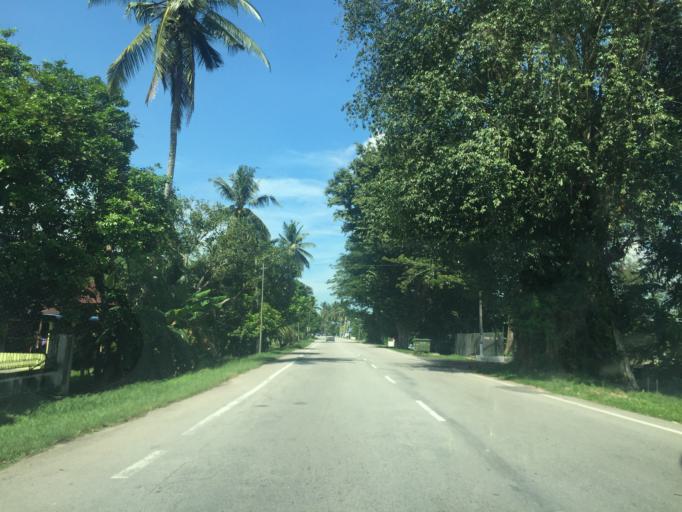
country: MY
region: Penang
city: Tasek Glugor
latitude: 5.4862
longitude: 100.4797
